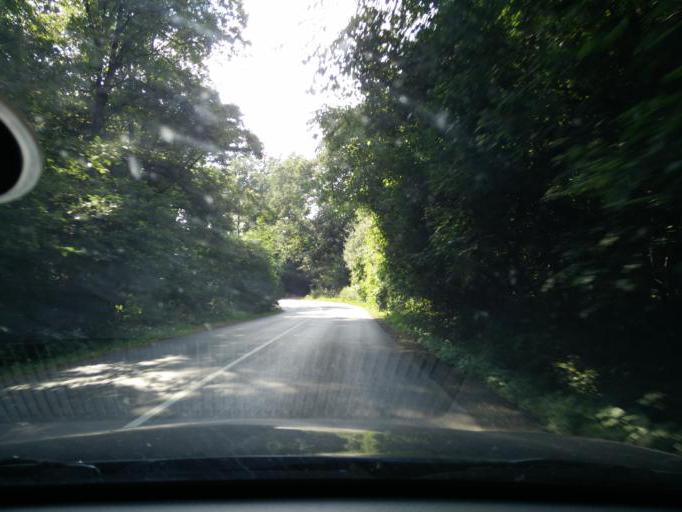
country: HU
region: Komarom-Esztergom
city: Tardos
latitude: 47.6627
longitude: 18.4094
